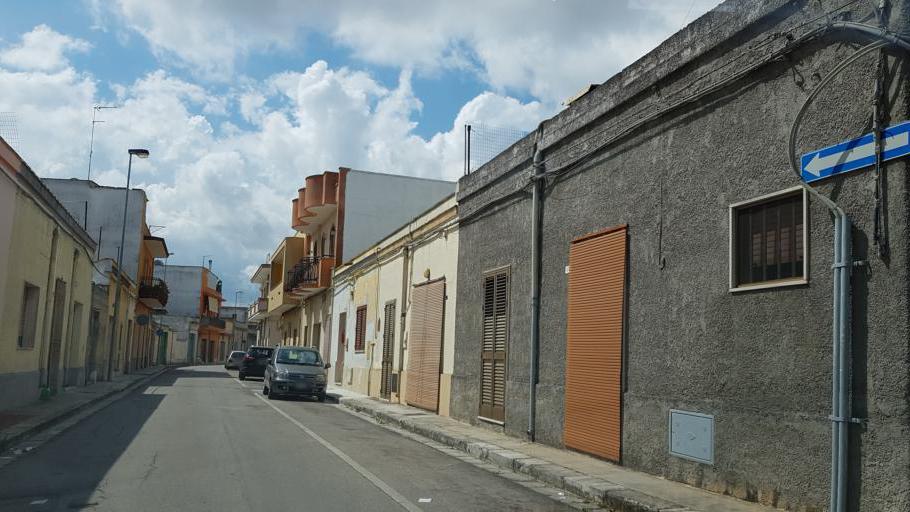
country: IT
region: Apulia
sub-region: Provincia di Brindisi
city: Mesagne
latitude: 40.5562
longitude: 17.8195
